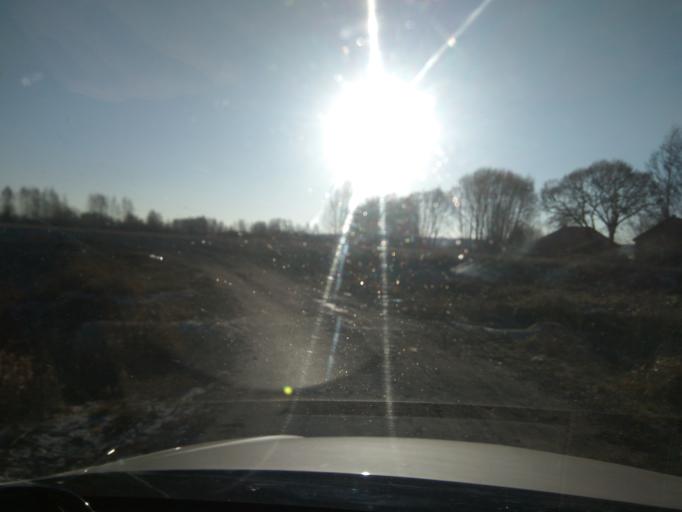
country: LV
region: Kuldigas Rajons
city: Kuldiga
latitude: 56.9611
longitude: 21.9618
